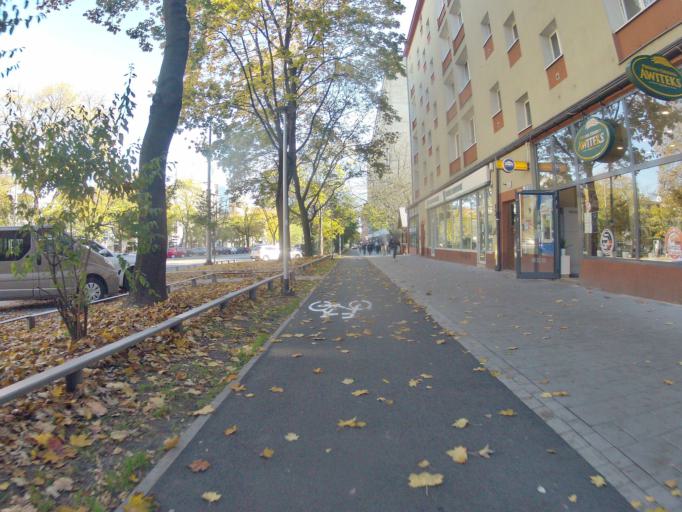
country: PL
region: Lesser Poland Voivodeship
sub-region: Krakow
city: Krakow
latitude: 50.0739
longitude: 19.9109
